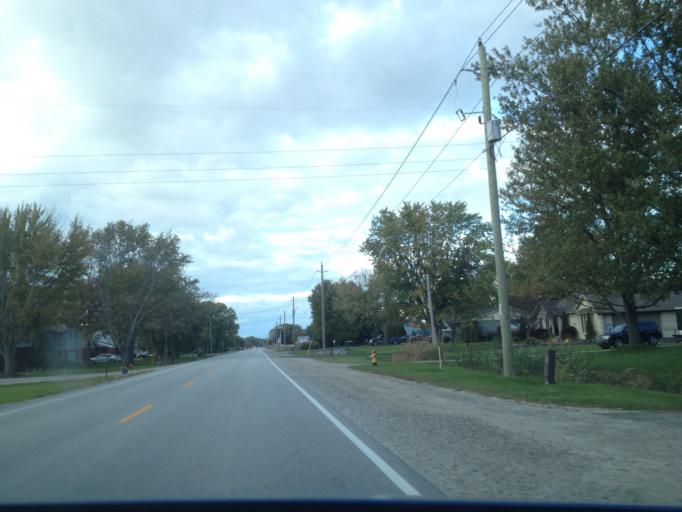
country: US
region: Michigan
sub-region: Wayne County
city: Grosse Pointe Farms
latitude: 42.2632
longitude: -82.7135
